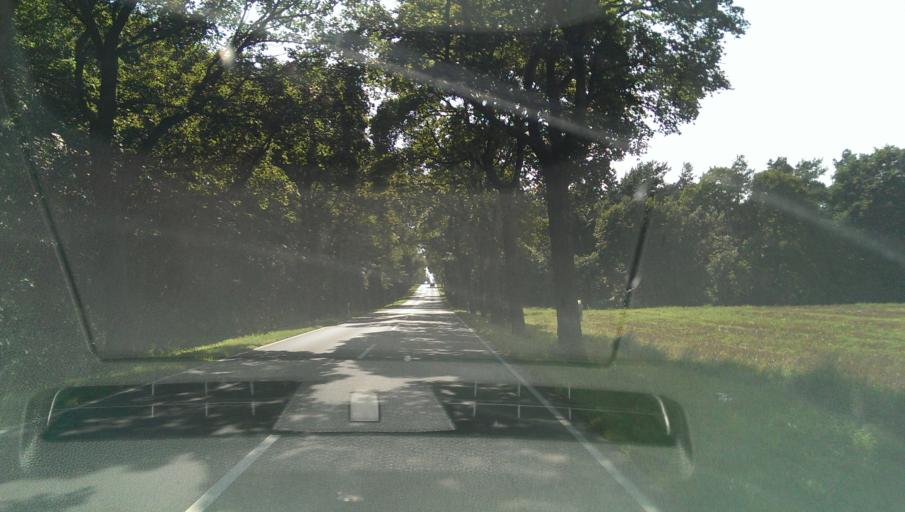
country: DE
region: Saxony-Anhalt
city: Abtsdorf
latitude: 51.9038
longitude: 12.6792
